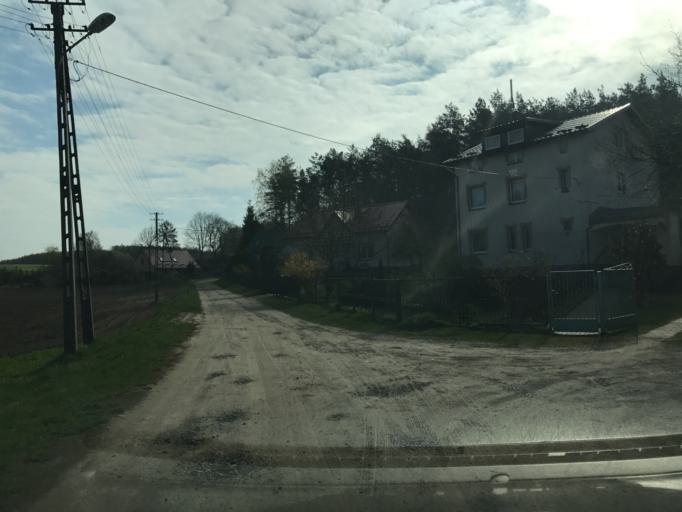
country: PL
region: Warmian-Masurian Voivodeship
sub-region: Powiat ostrodzki
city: Dabrowno
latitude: 53.3869
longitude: 20.0040
